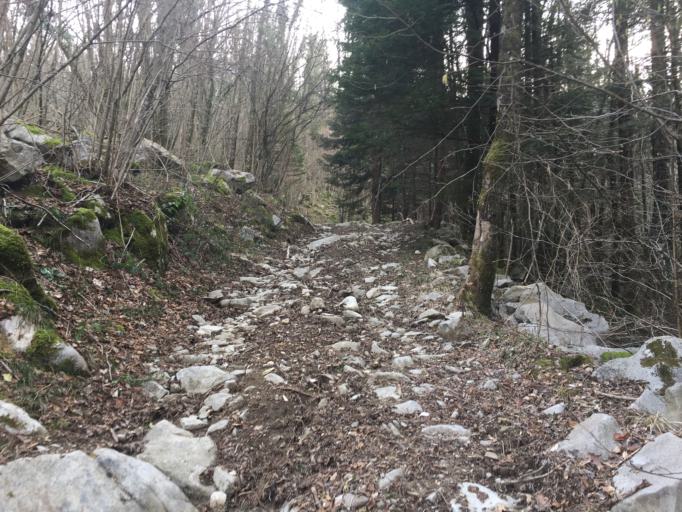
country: IT
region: Friuli Venezia Giulia
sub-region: Provincia di Udine
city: Lusevera
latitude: 46.2625
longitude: 13.3015
